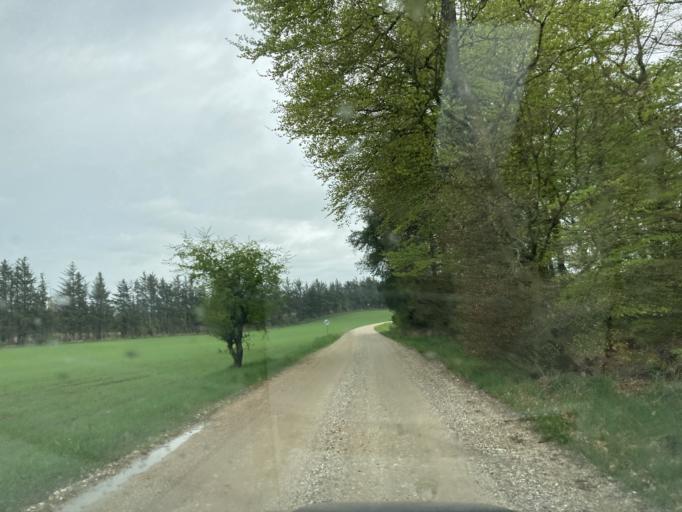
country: DK
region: North Denmark
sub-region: Thisted Kommune
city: Hanstholm
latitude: 57.0233
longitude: 8.5930
